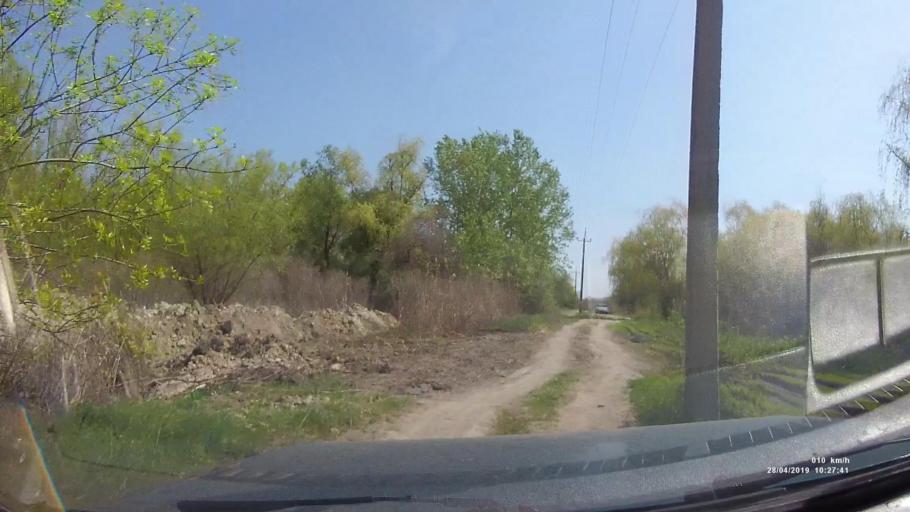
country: RU
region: Rostov
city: Azov
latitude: 47.1150
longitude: 39.4468
